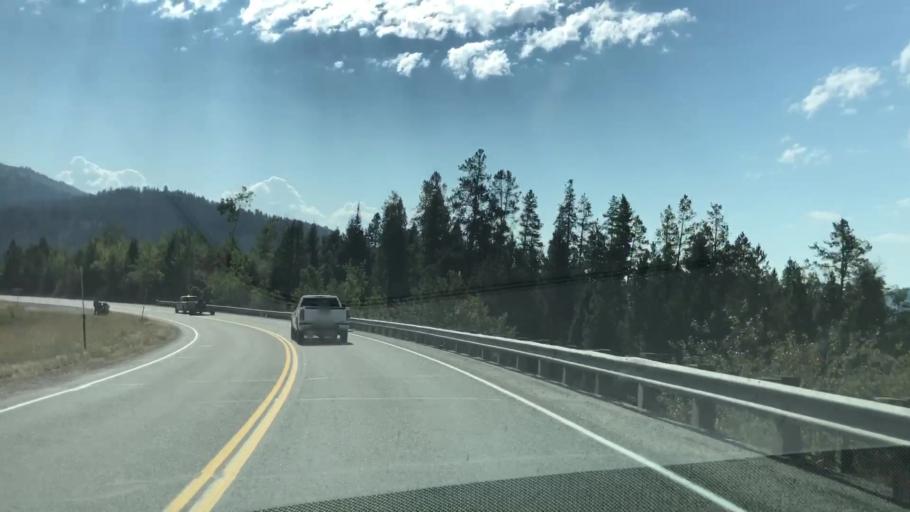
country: US
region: Wyoming
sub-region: Teton County
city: Hoback
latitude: 43.2513
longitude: -111.1166
